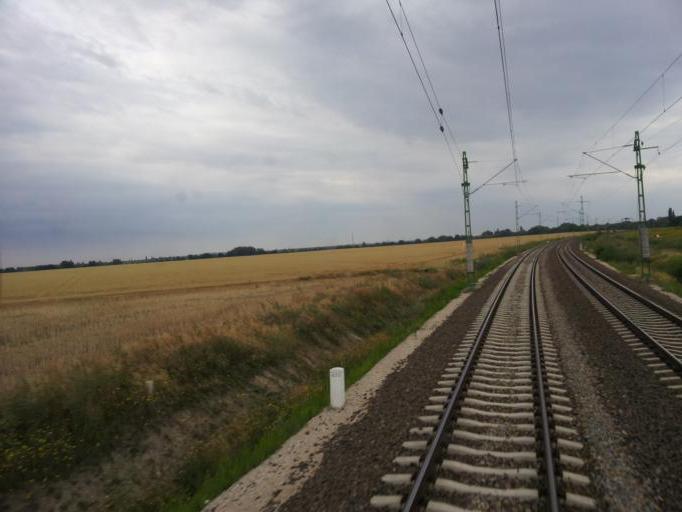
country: HU
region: Fejer
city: Szekesfehervar
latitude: 47.1701
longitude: 18.4775
